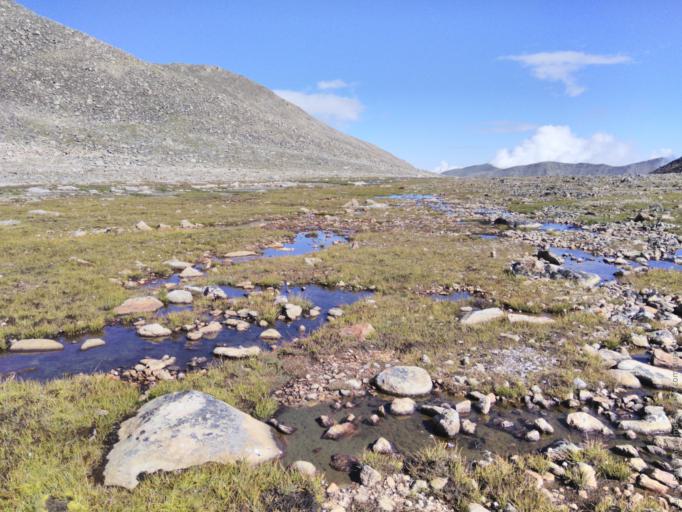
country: RU
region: Kabardino-Balkariya
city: Terskol
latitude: 43.3707
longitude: 42.3491
